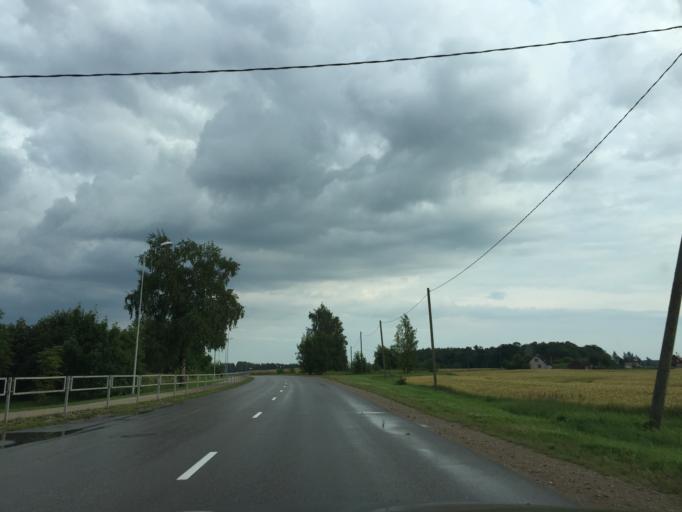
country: LV
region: Dobeles Rajons
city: Dobele
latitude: 56.6061
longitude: 23.2757
